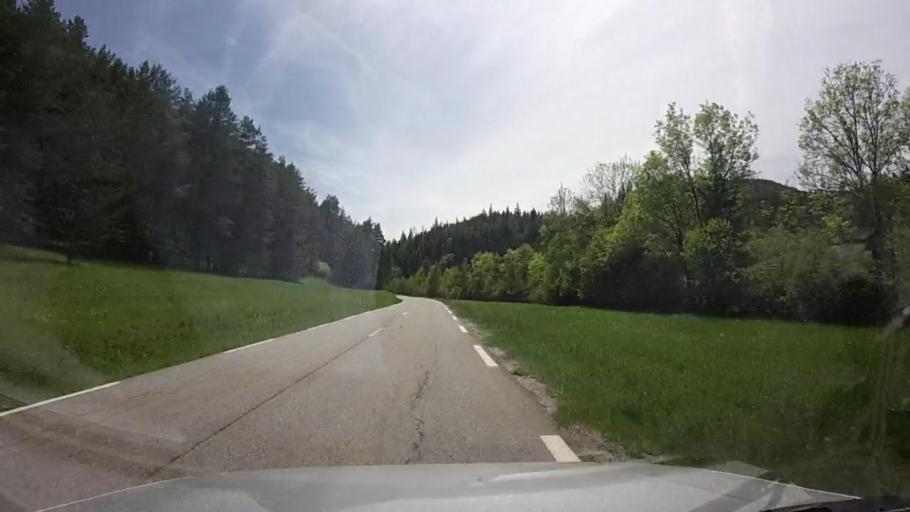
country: FR
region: Provence-Alpes-Cote d'Azur
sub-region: Departement des Alpes-de-Haute-Provence
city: Seyne-les-Alpes
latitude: 44.2540
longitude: 6.3674
